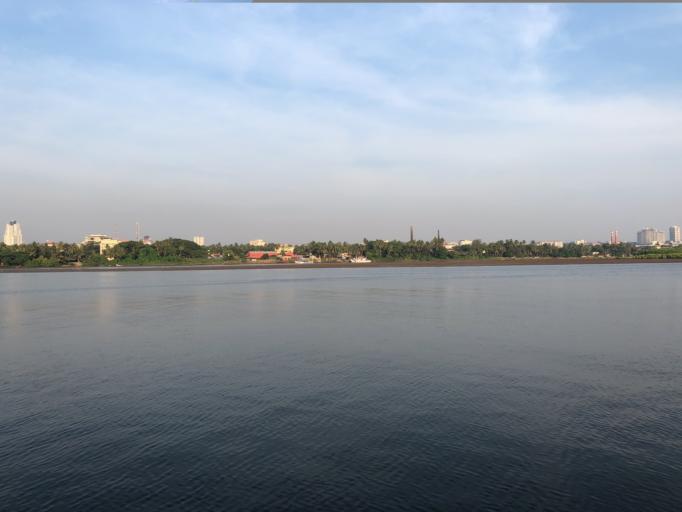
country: IN
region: Karnataka
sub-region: Dakshina Kannada
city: Mangalore
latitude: 12.8807
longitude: 74.8199
